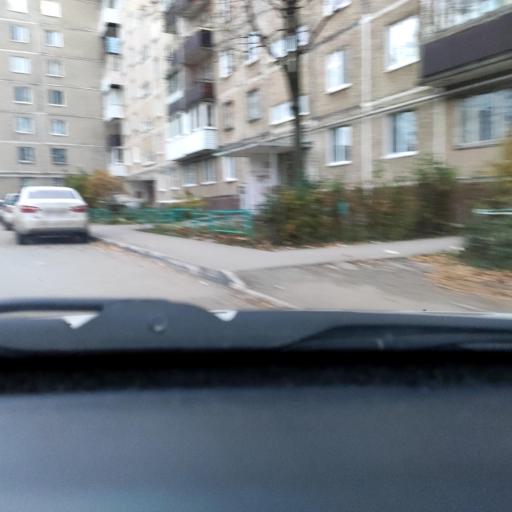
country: RU
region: Perm
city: Perm
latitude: 57.9648
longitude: 56.2133
